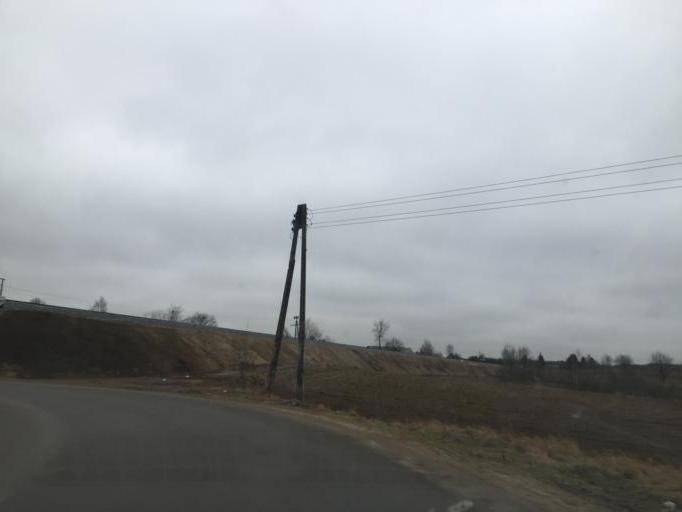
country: PL
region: Pomeranian Voivodeship
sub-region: Powiat kartuski
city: Banino
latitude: 54.3965
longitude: 18.4326
